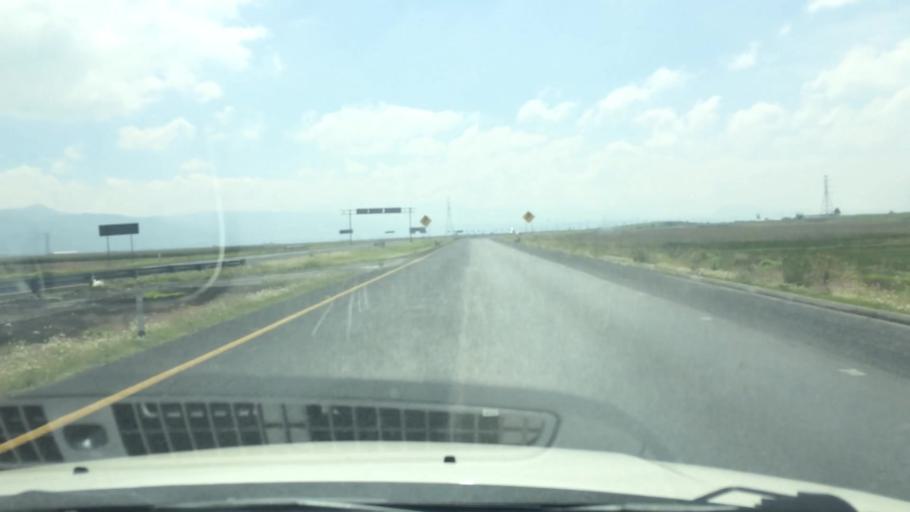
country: MX
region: Mexico
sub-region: Toluca
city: La Constitucion Toltepec
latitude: 19.3699
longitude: -99.5433
